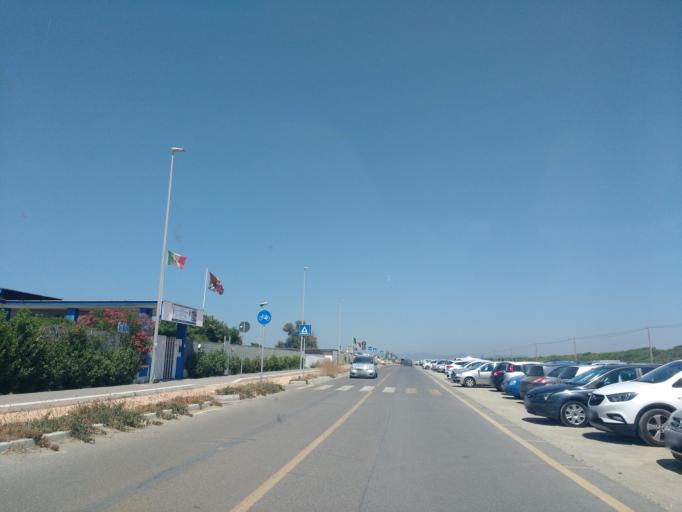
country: IT
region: Latium
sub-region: Citta metropolitana di Roma Capitale
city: Passo Oscuro
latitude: 41.8791
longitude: 12.1754
